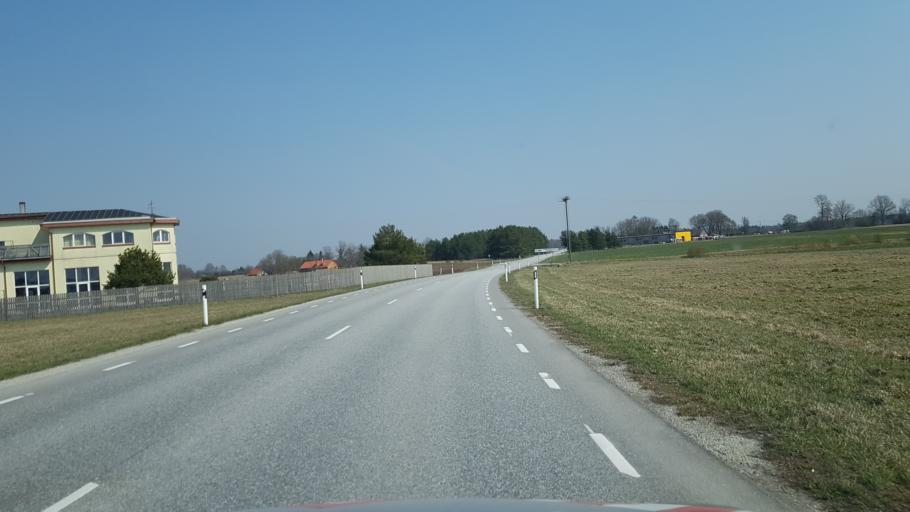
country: EE
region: Harju
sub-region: Saku vald
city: Saku
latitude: 59.2668
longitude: 24.7268
